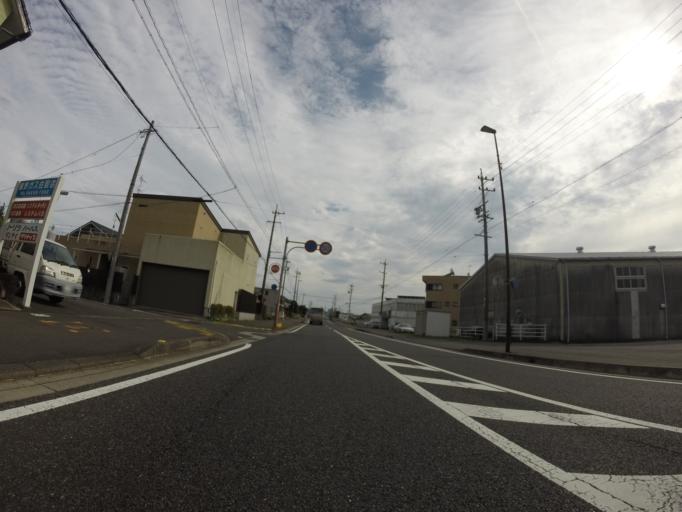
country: JP
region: Shizuoka
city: Shizuoka-shi
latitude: 35.0414
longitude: 138.4977
